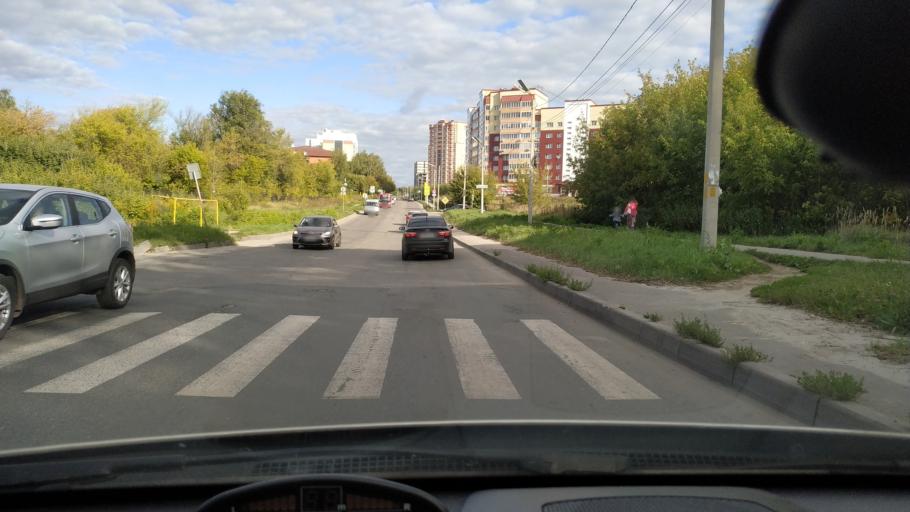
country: RU
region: Rjazan
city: Ryazan'
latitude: 54.6060
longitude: 39.7315
